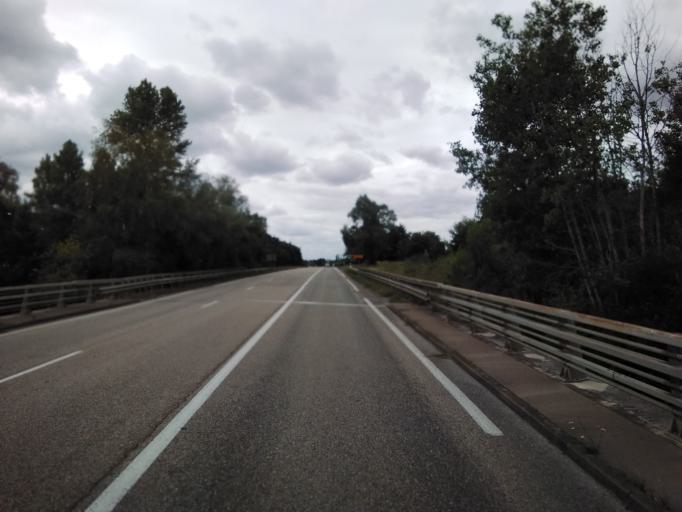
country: FR
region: Rhone-Alpes
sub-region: Departement de l'Ain
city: Saint-Etienne-du-Bois
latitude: 46.2438
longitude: 5.2687
